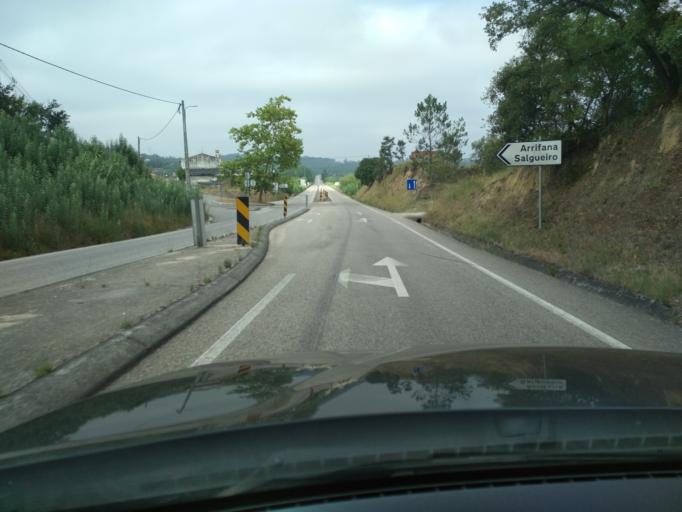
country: PT
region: Coimbra
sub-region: Condeixa-A-Nova
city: Condeixa-a-Nova
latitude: 40.1021
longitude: -8.5066
